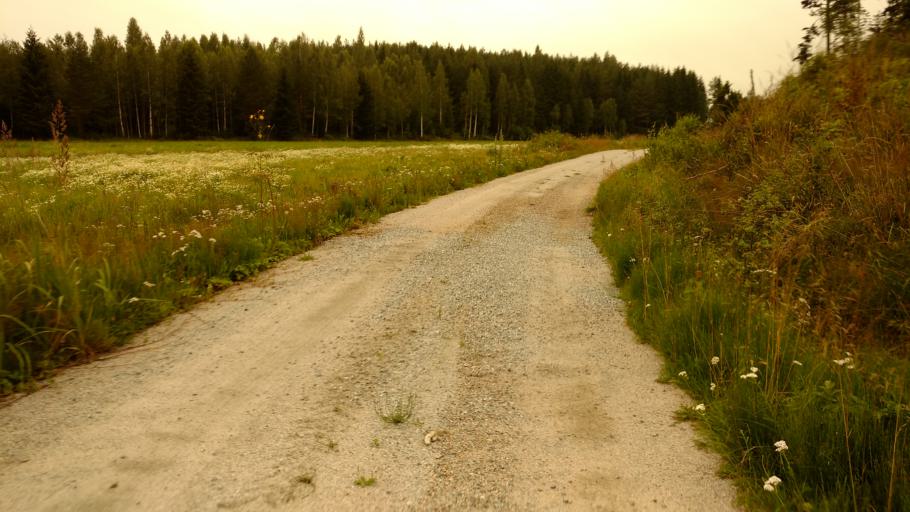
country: FI
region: Varsinais-Suomi
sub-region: Salo
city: Pertteli
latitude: 60.4045
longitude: 23.2278
